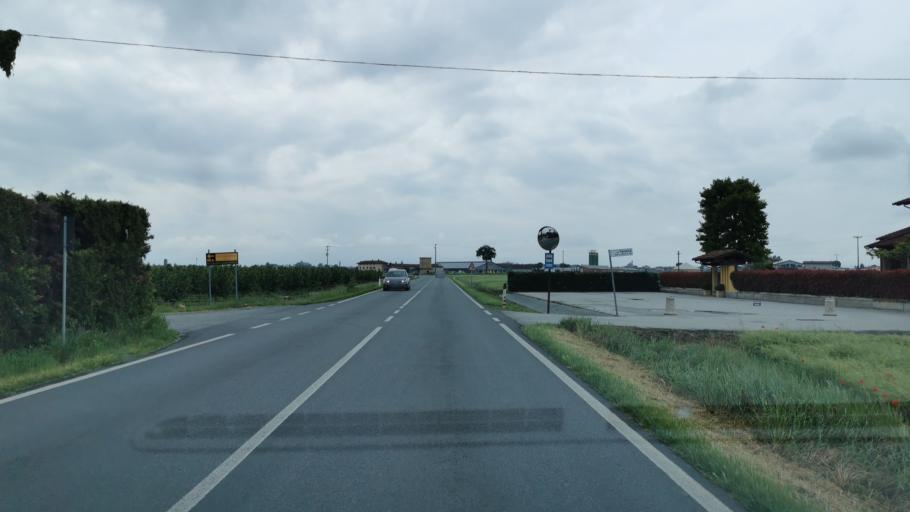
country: IT
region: Piedmont
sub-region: Provincia di Cuneo
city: Villafalletto
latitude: 44.5660
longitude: 7.5303
